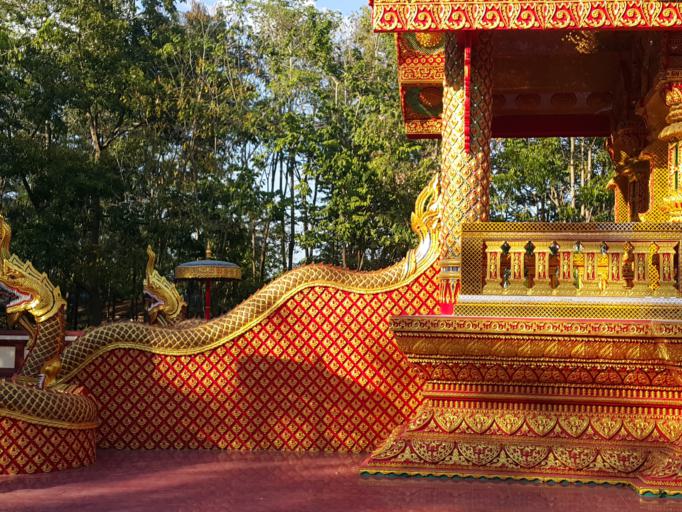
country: TH
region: Sukhothai
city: Thung Saliam
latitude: 17.3224
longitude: 99.5524
